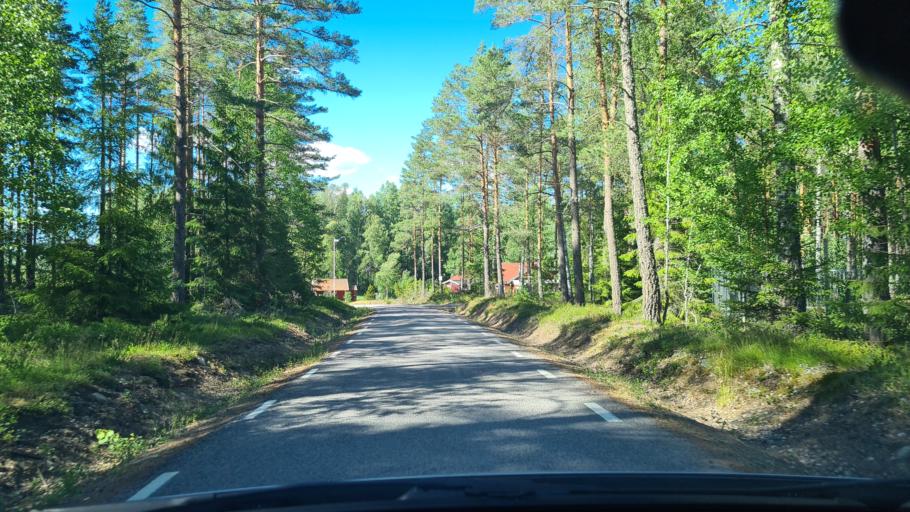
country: SE
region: OEstergoetland
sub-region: Norrkopings Kommun
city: Krokek
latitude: 58.7140
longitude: 16.4292
